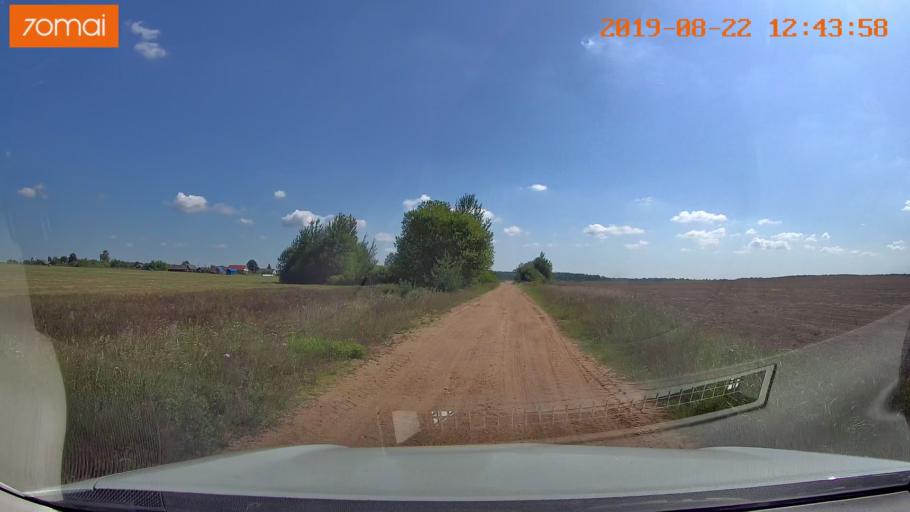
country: BY
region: Minsk
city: Prawdzinski
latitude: 53.4509
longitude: 27.6057
